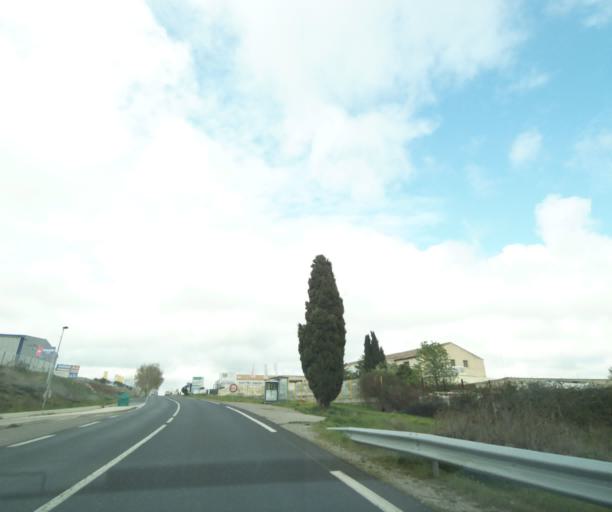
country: FR
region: Languedoc-Roussillon
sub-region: Departement de l'Herault
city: Fabregues
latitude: 43.5566
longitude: 3.7937
